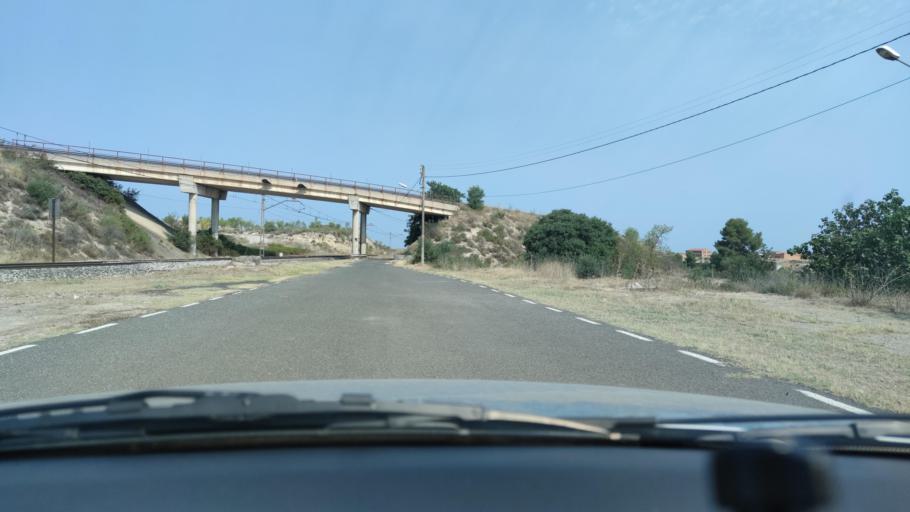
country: ES
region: Catalonia
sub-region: Provincia de Lleida
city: Arbeca
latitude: 41.5047
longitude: 0.9240
